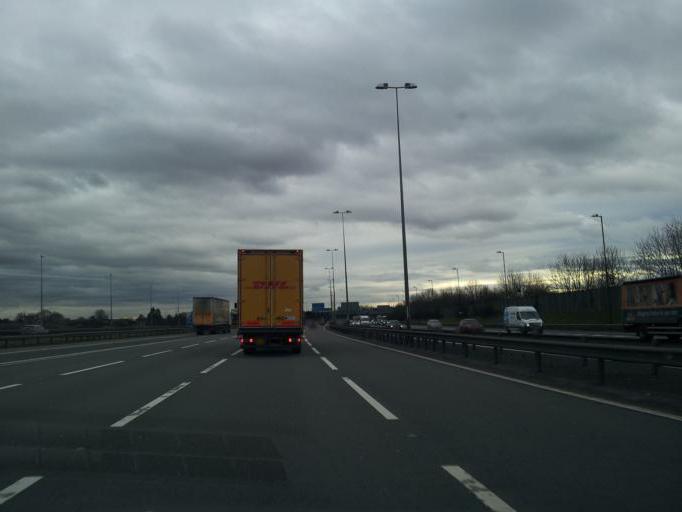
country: GB
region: England
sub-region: Warwickshire
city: Water Orton
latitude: 52.5161
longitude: -1.7254
